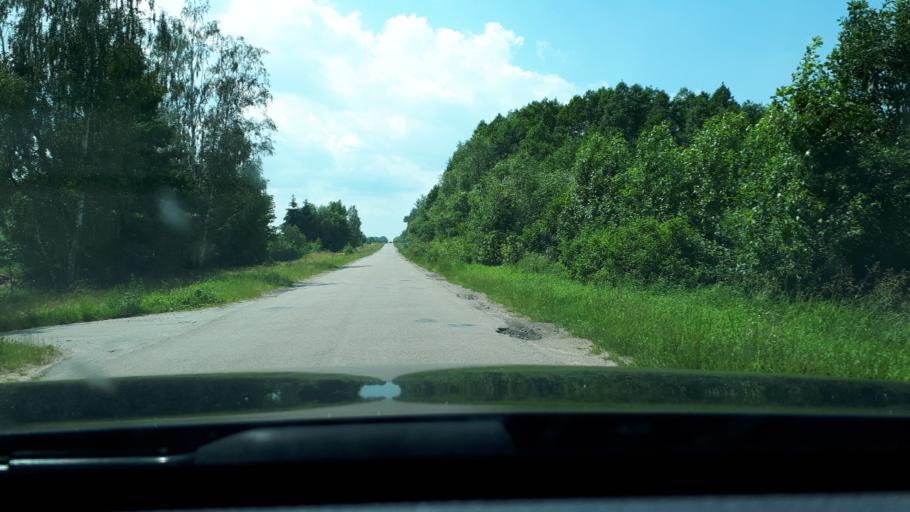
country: PL
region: Podlasie
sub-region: Powiat bialostocki
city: Choroszcz
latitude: 53.1241
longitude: 22.9473
